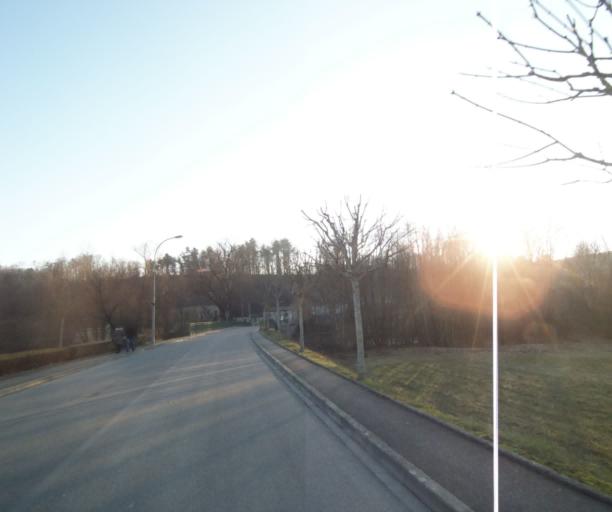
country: FR
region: Champagne-Ardenne
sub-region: Departement de la Haute-Marne
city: Bienville
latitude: 48.5490
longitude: 5.0746
